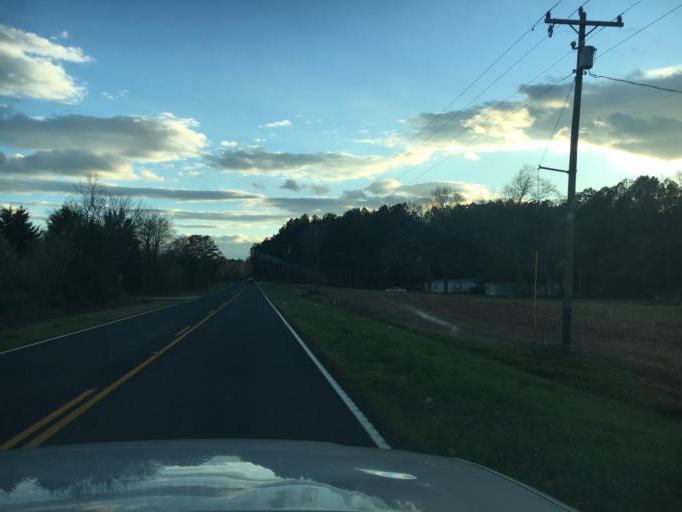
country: US
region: South Carolina
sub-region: Greenwood County
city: Greenwood
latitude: 34.1120
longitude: -82.1815
